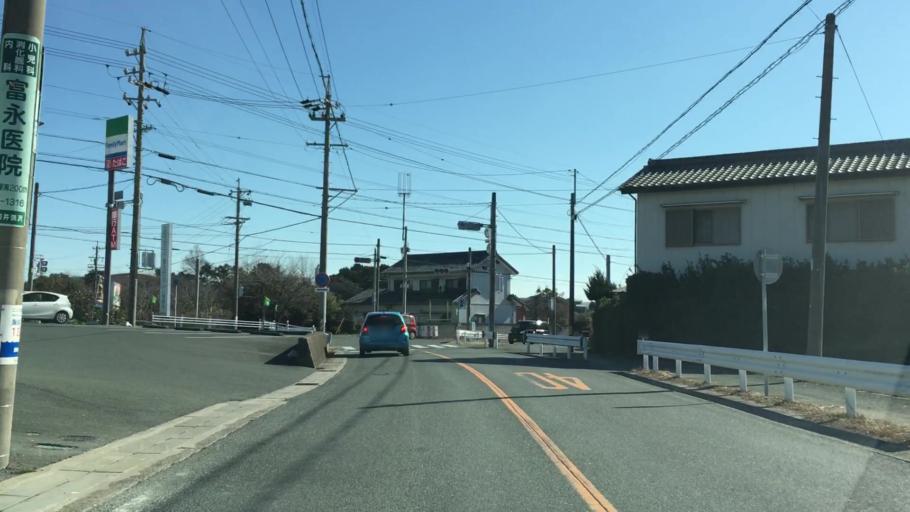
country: JP
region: Aichi
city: Tahara
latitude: 34.6960
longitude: 137.2767
